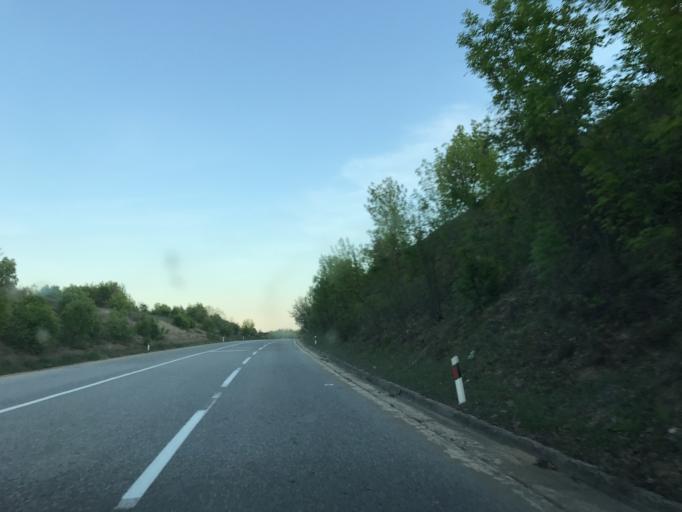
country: RO
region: Mehedinti
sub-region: Comuna Gogosu
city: Ostrovu Mare
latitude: 44.4236
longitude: 22.4788
